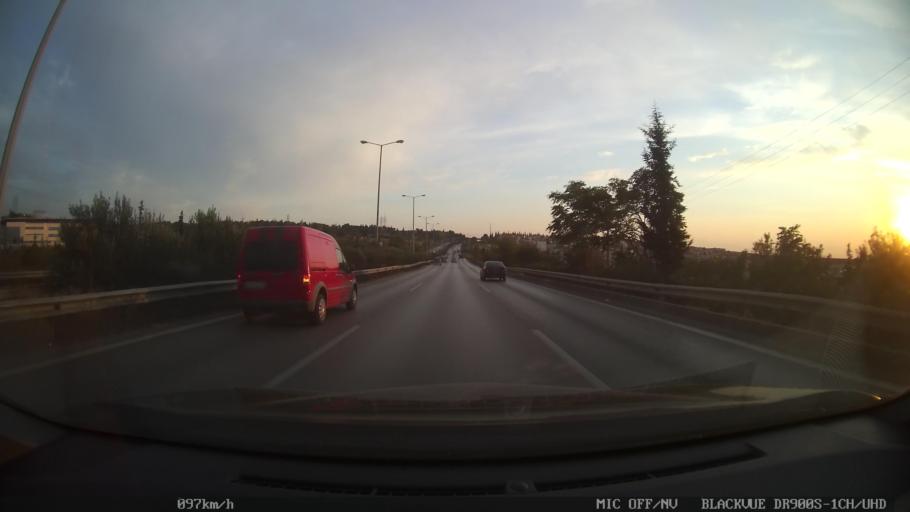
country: GR
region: Central Macedonia
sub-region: Nomos Thessalonikis
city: Pylaia
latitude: 40.6062
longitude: 22.9993
